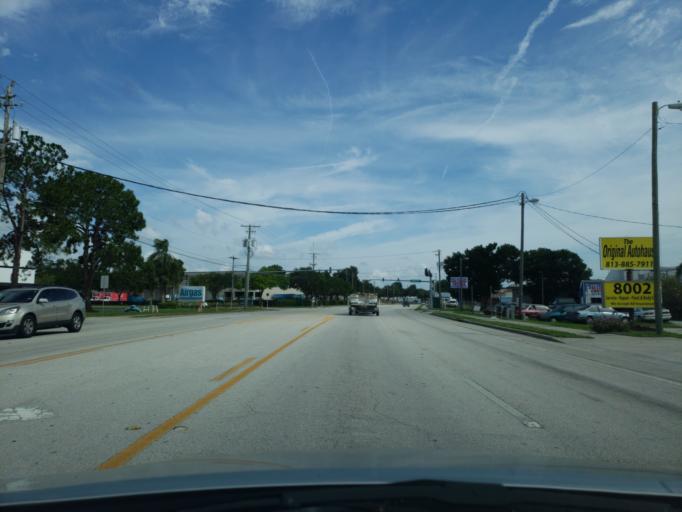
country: US
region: Florida
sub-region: Hillsborough County
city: Egypt Lake-Leto
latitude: 28.0208
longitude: -82.5347
